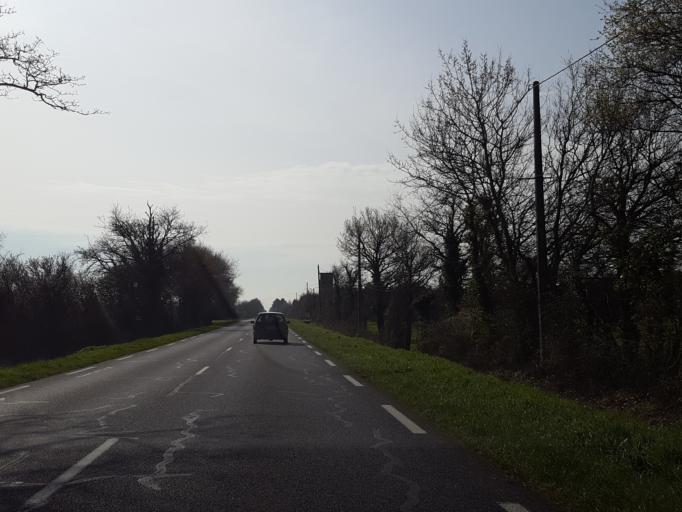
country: FR
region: Pays de la Loire
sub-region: Departement de la Vendee
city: Saligny
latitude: 46.8158
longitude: -1.4652
